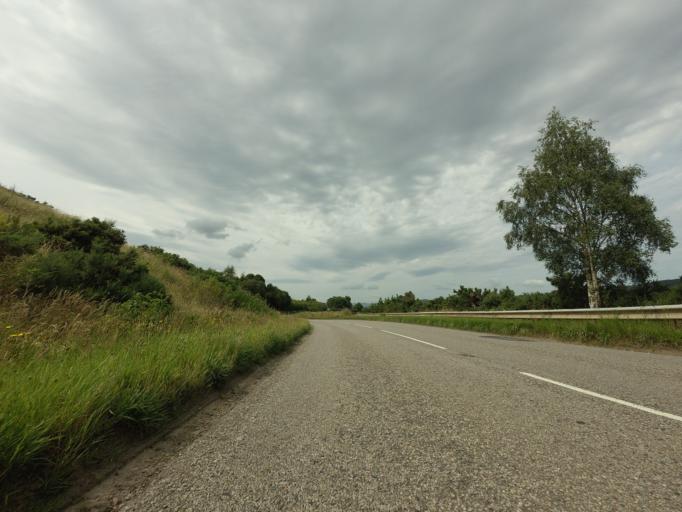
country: GB
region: Scotland
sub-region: Highland
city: Alness
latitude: 57.8601
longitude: -4.3147
